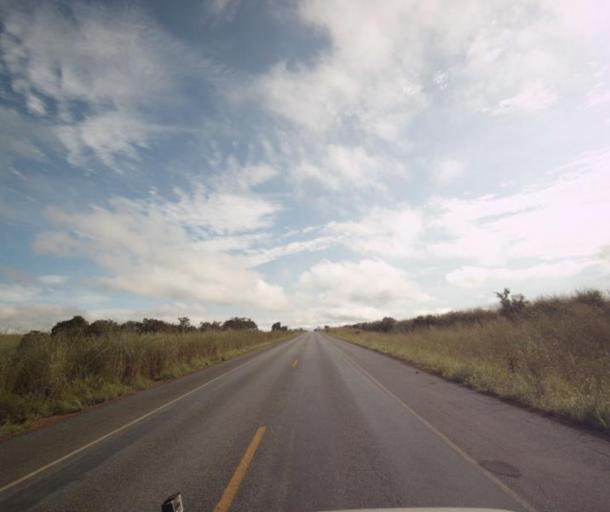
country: BR
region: Goias
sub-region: Padre Bernardo
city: Padre Bernardo
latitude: -15.4730
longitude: -48.6149
